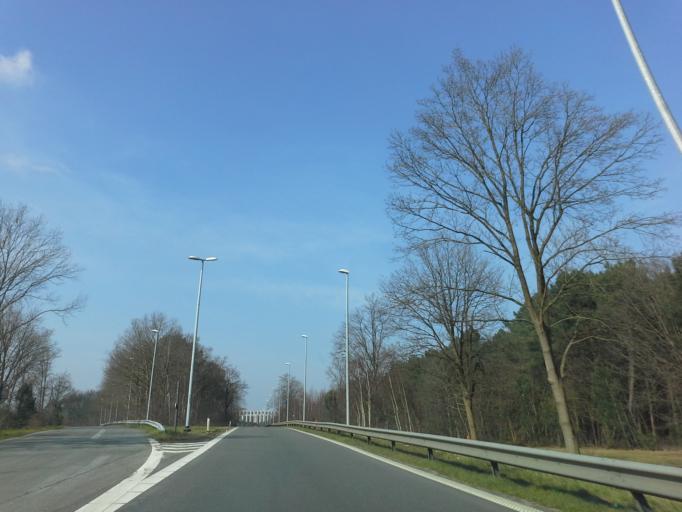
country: BE
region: Flanders
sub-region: Provincie Antwerpen
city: Laakdal
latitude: 51.1066
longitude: 5.0276
